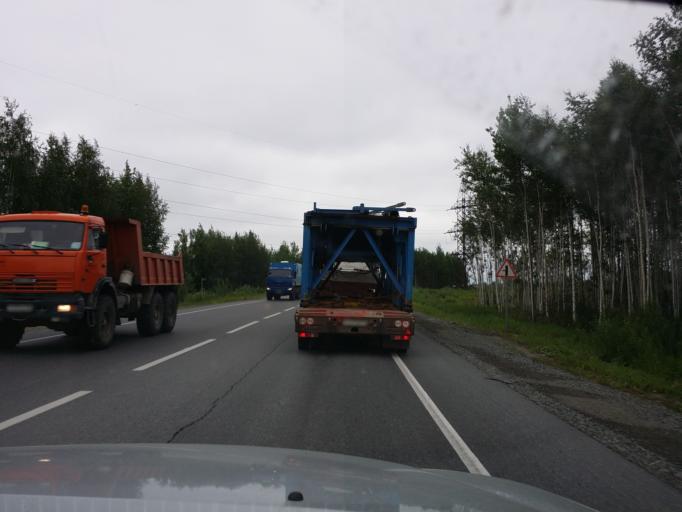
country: RU
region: Khanty-Mansiyskiy Avtonomnyy Okrug
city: Nizhnevartovsk
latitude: 61.0257
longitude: 76.3676
